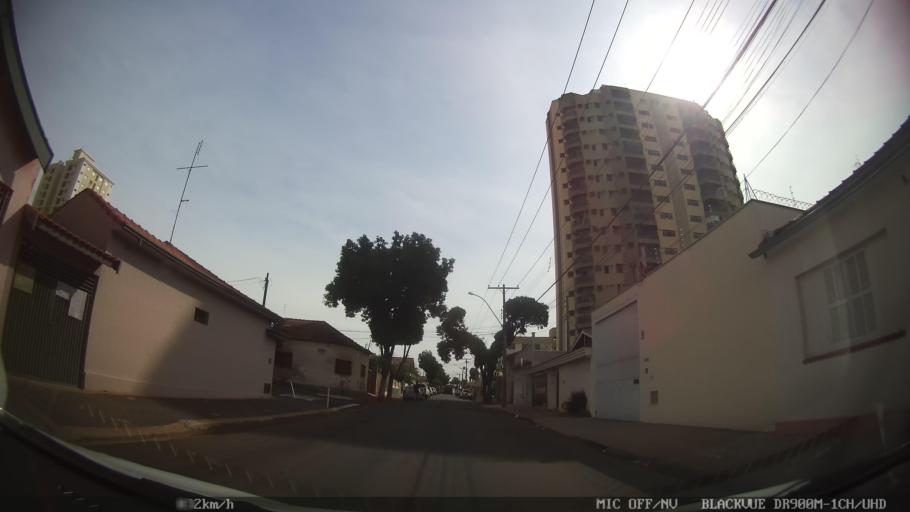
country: BR
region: Sao Paulo
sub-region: Piracicaba
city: Piracicaba
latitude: -22.7374
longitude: -47.6550
